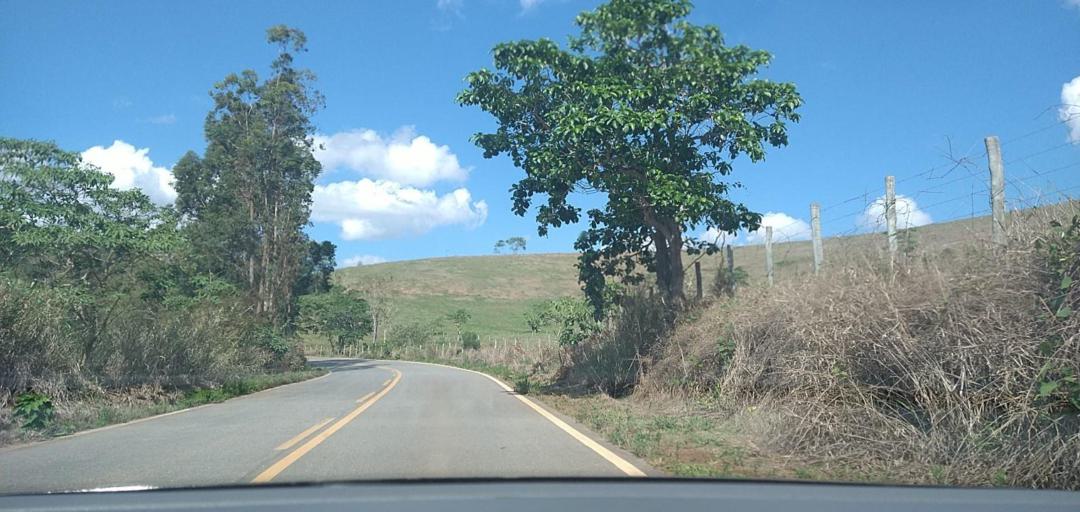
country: BR
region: Minas Gerais
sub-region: Alvinopolis
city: Alvinopolis
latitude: -20.0165
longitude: -43.0887
